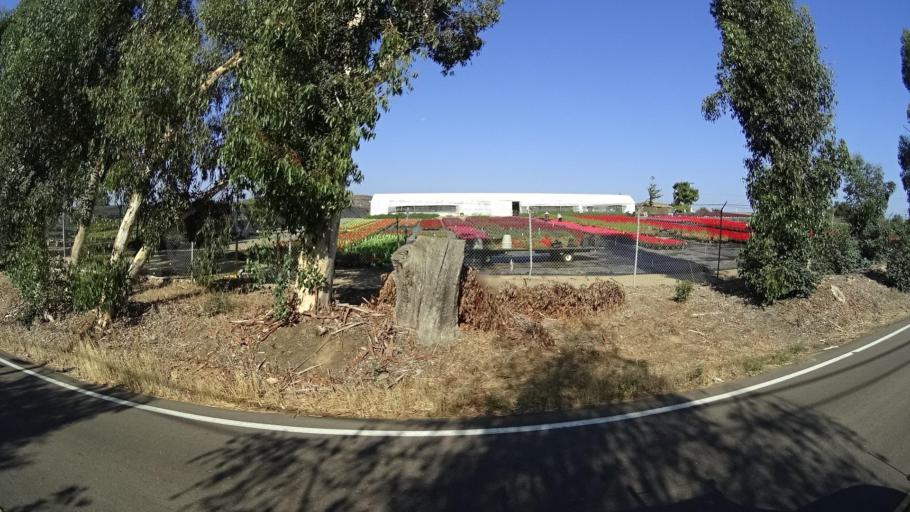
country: US
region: California
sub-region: San Diego County
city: Fallbrook
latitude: 33.3388
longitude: -117.2449
